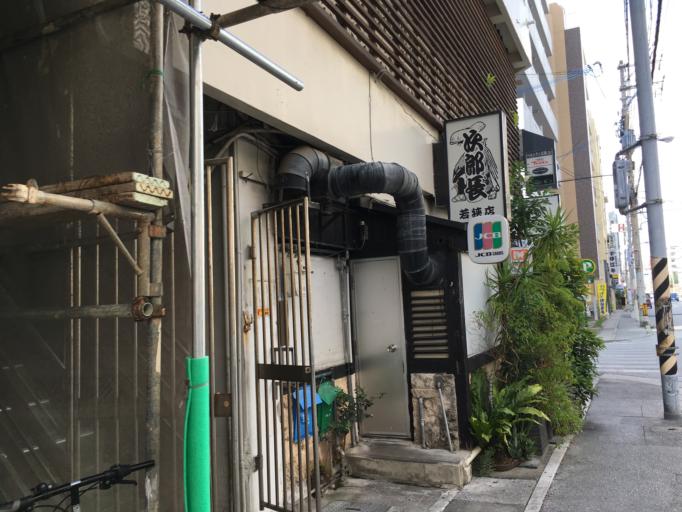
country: JP
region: Okinawa
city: Naha-shi
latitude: 26.2203
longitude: 127.6767
